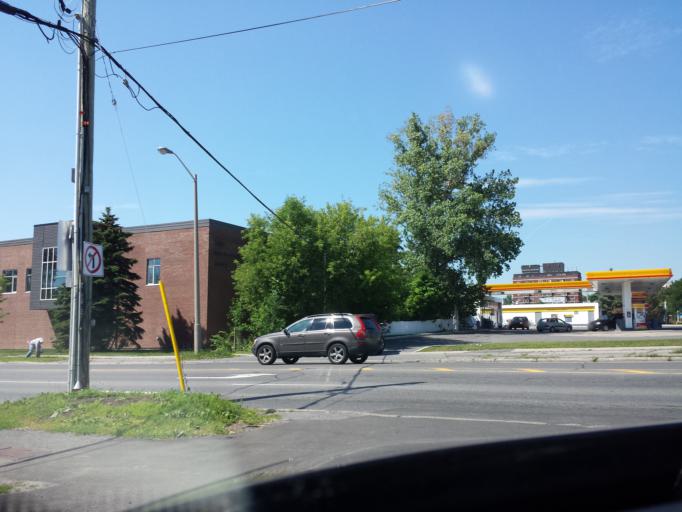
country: CA
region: Ontario
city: Bells Corners
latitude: 45.3688
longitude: -75.7723
